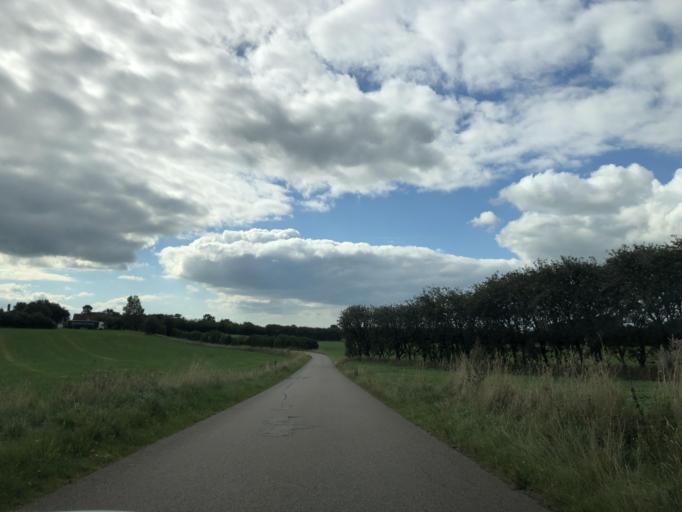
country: DK
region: North Denmark
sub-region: Vesthimmerland Kommune
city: Aars
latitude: 56.8176
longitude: 9.6549
